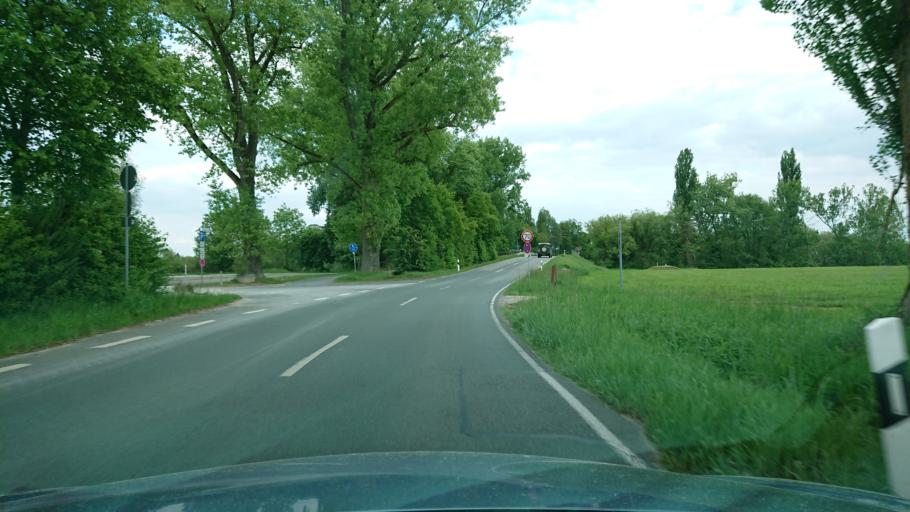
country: DE
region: Bavaria
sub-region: Regierungsbezirk Mittelfranken
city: Baiersdorf
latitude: 49.6591
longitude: 11.0228
